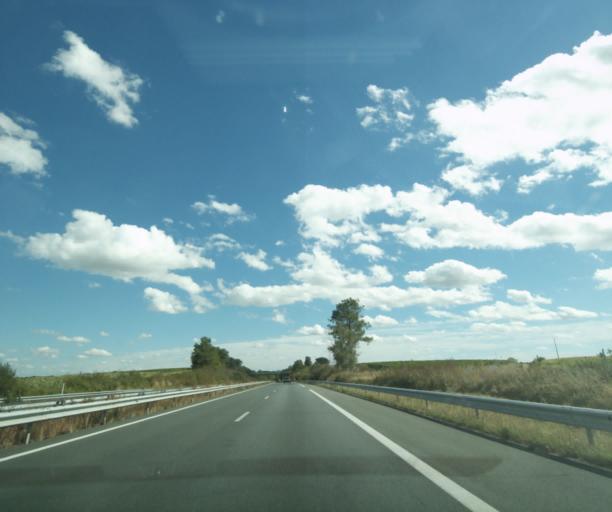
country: FR
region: Aquitaine
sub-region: Departement du Lot-et-Garonne
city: Meilhan-sur-Garonne
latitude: 44.4651
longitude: 0.0670
